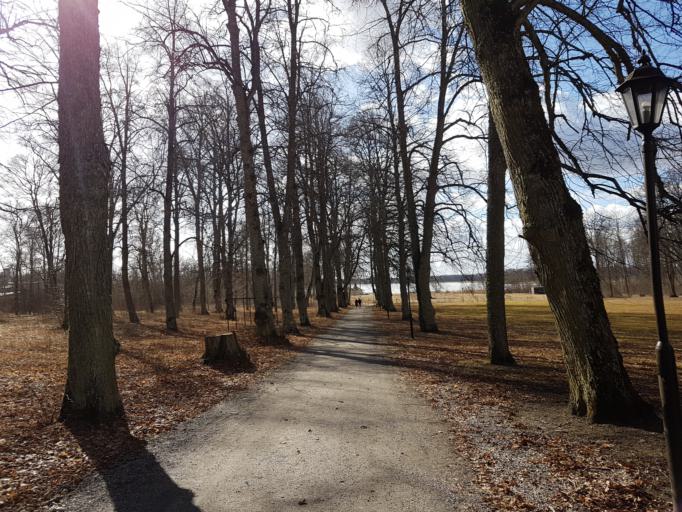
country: SE
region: Stockholm
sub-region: Norrtalje Kommun
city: Nykvarn
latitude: 59.7905
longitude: 18.2954
